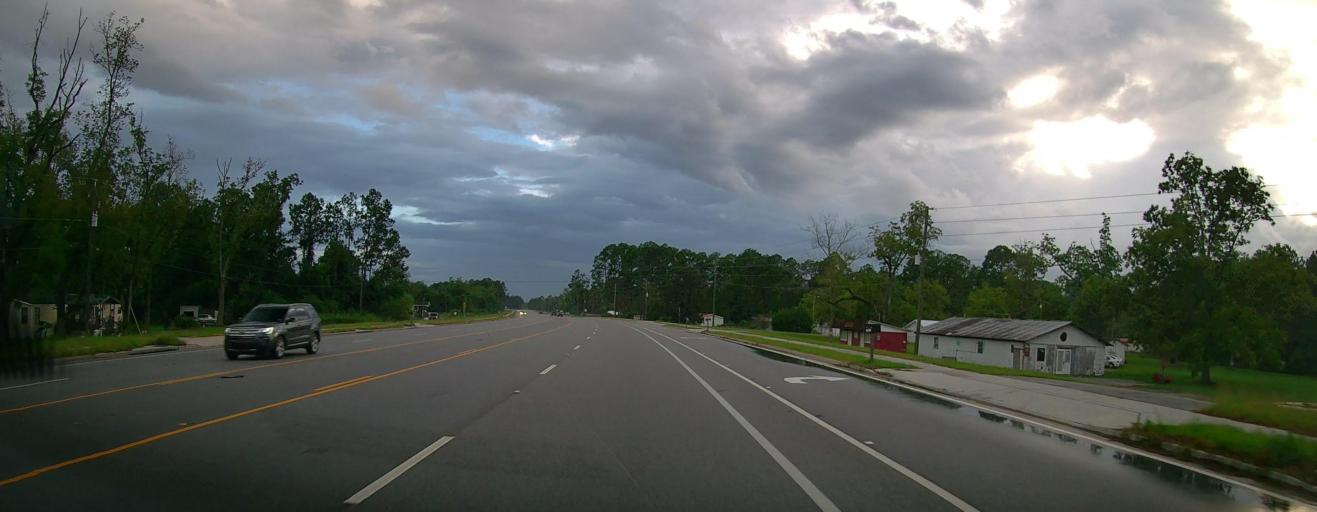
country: US
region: Georgia
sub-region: Ware County
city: Deenwood
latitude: 31.1841
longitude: -82.3957
